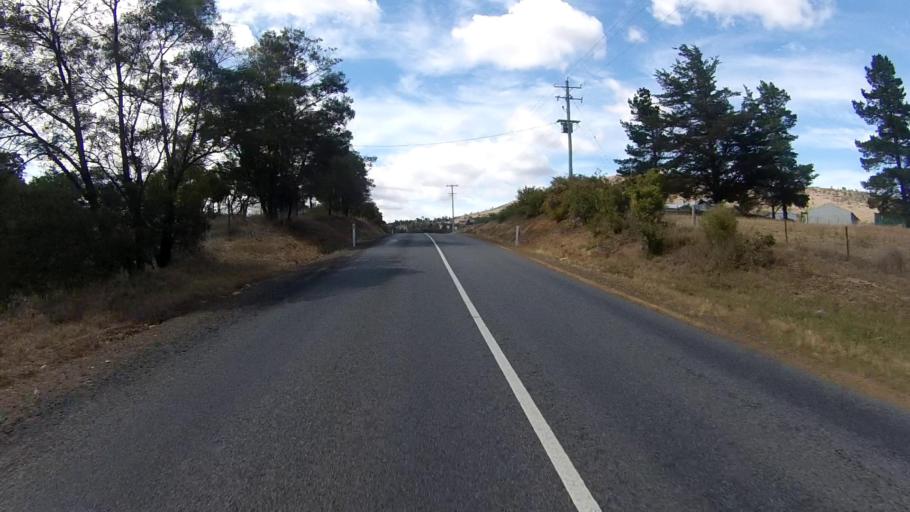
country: AU
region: Tasmania
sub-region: Brighton
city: Bridgewater
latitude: -42.7208
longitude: 147.2797
